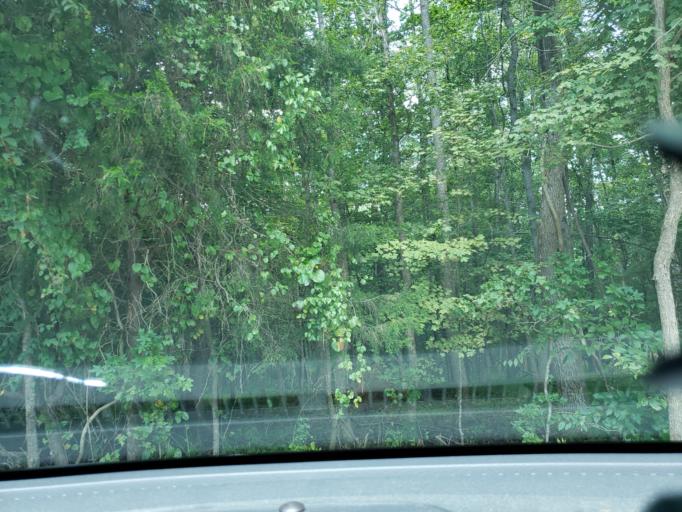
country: US
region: North Carolina
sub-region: Orange County
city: Hillsborough
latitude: 36.0780
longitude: -79.0072
